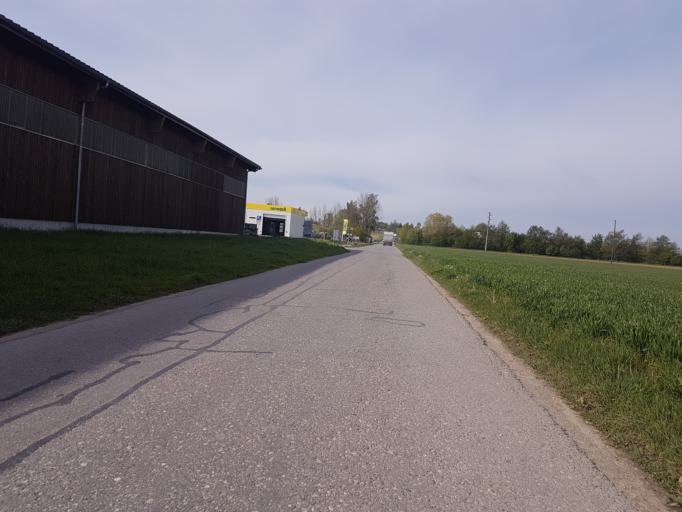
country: CH
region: Bern
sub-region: Biel/Bienne District
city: Bellmund
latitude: 47.1103
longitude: 7.2243
